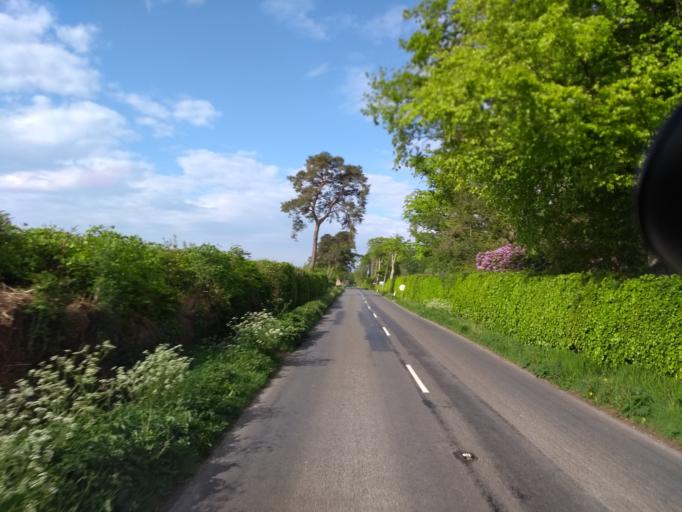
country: GB
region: England
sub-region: Dorset
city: Lyme Regis
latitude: 50.7797
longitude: -2.9369
